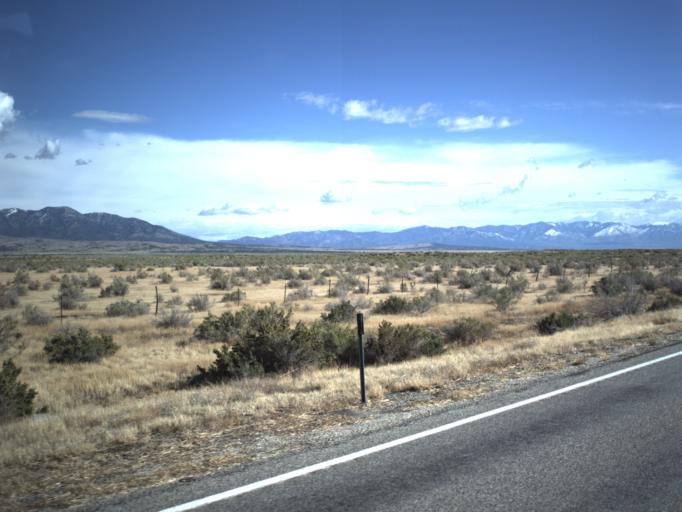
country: US
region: Utah
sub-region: Millard County
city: Delta
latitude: 39.3157
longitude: -112.4795
